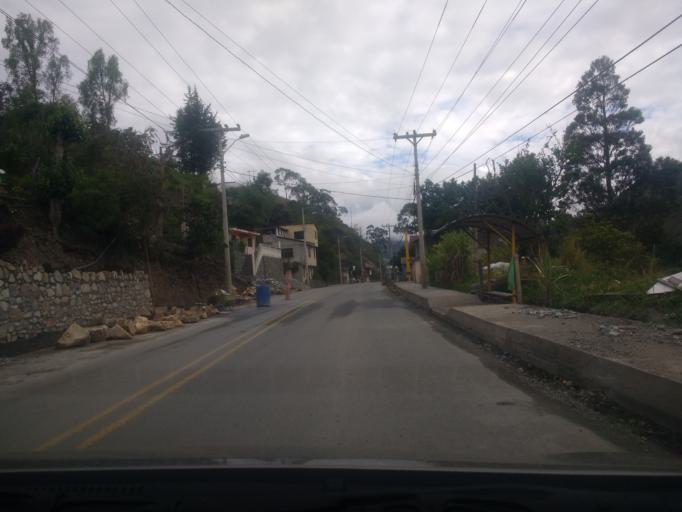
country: EC
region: Azuay
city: La Union
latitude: -2.8280
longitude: -78.7714
